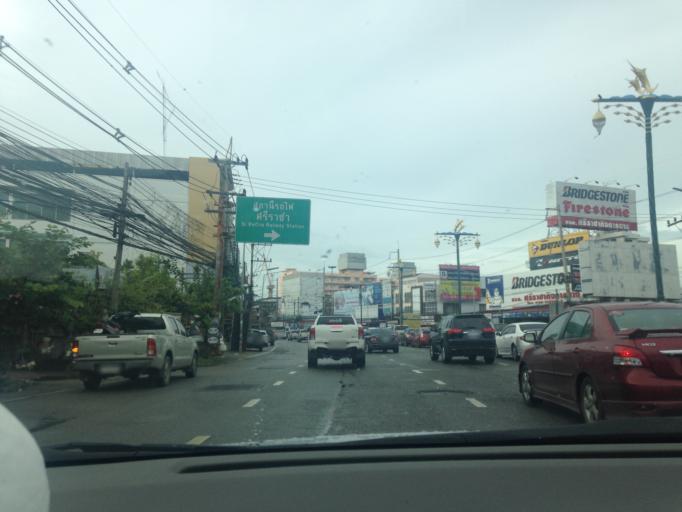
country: TH
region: Chon Buri
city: Si Racha
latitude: 13.1640
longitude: 100.9304
